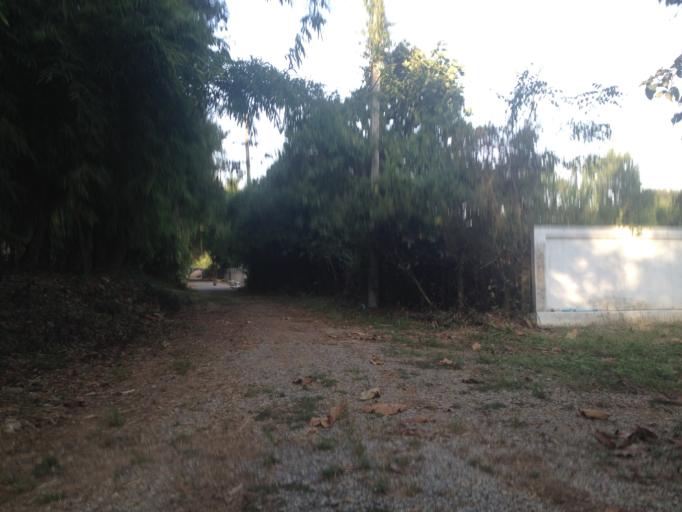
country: TH
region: Chiang Mai
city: Hang Dong
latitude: 18.7373
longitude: 98.9229
